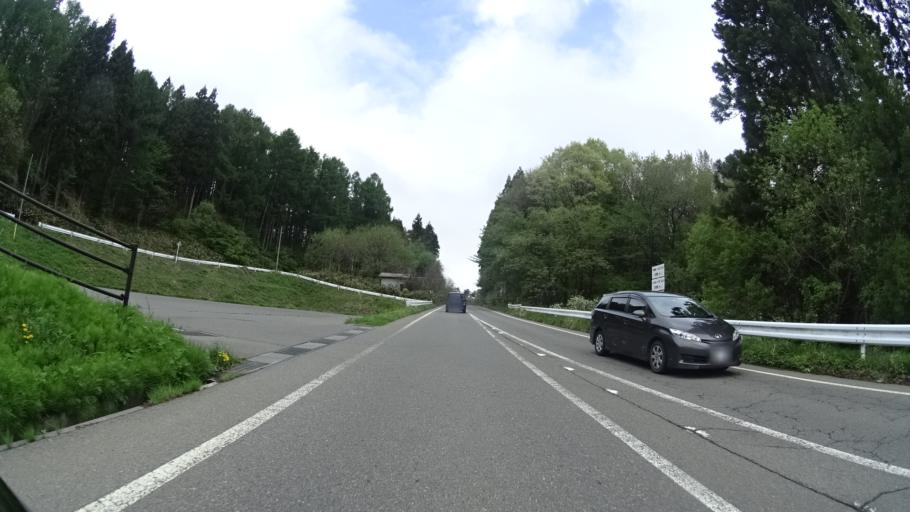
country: JP
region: Nagano
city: Nagano-shi
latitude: 36.7193
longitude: 138.2083
